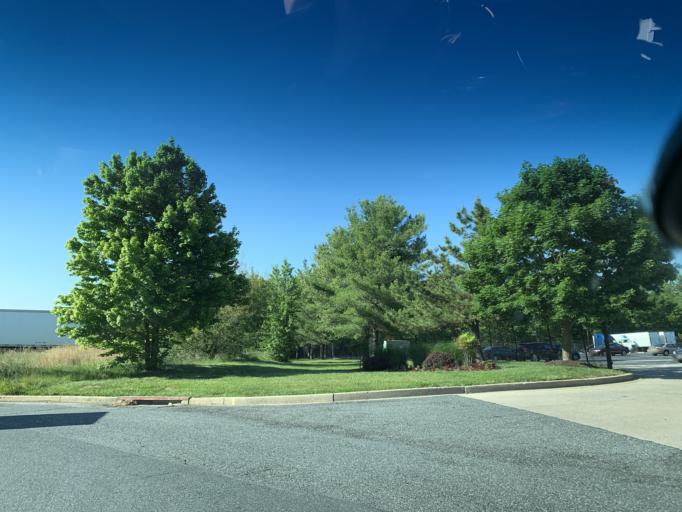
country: US
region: Maryland
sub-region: Harford County
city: Riverside
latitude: 39.4819
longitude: -76.2259
